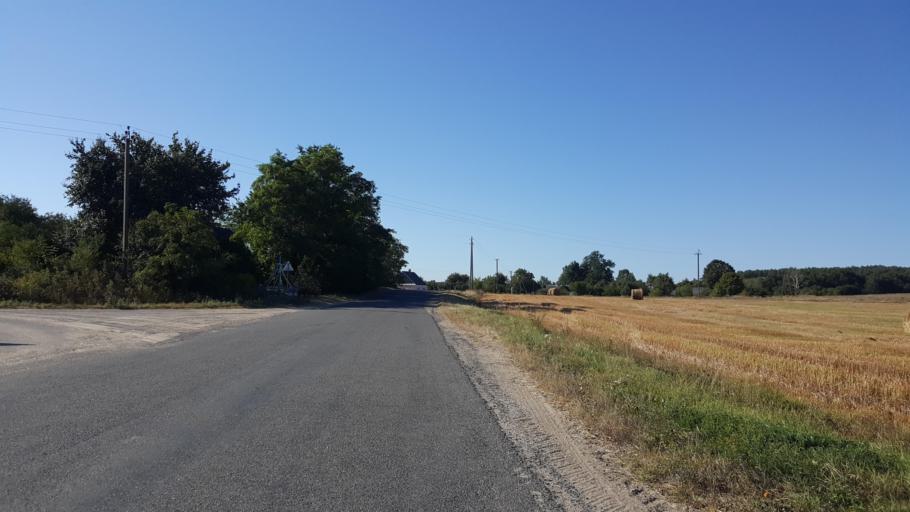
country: BY
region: Brest
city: Kamyanyets
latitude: 52.3853
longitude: 23.7464
